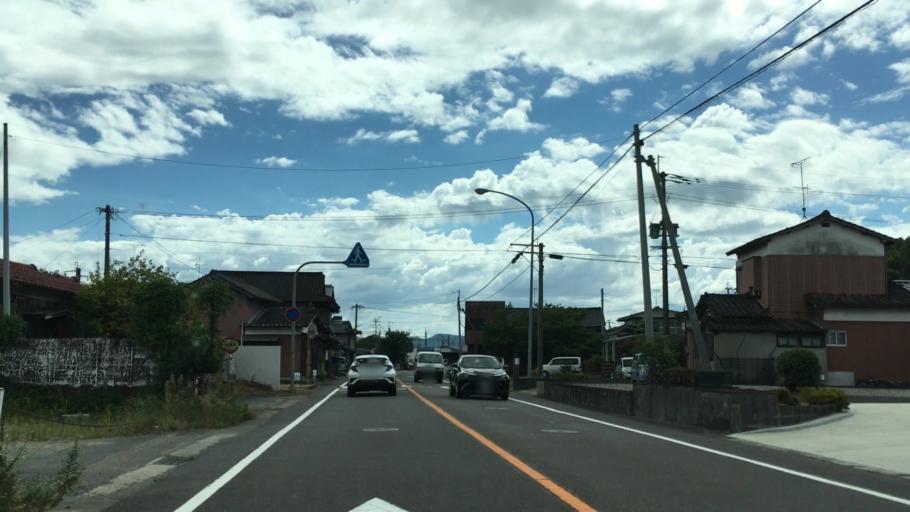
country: JP
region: Saga Prefecture
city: Saga-shi
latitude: 33.2215
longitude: 130.1710
